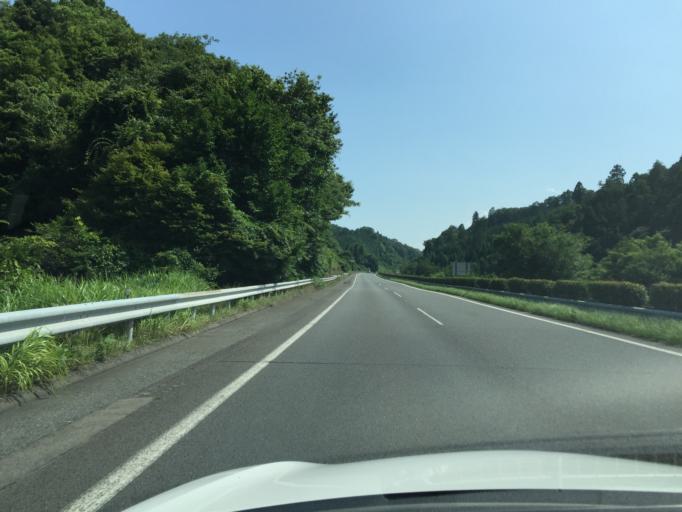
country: JP
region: Fukushima
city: Iwaki
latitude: 36.9958
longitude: 140.8062
